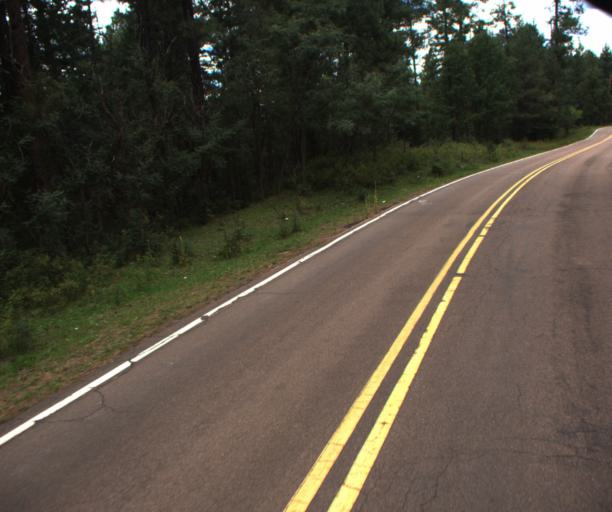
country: US
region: Arizona
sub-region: Navajo County
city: Pinetop-Lakeside
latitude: 34.0316
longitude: -109.7522
